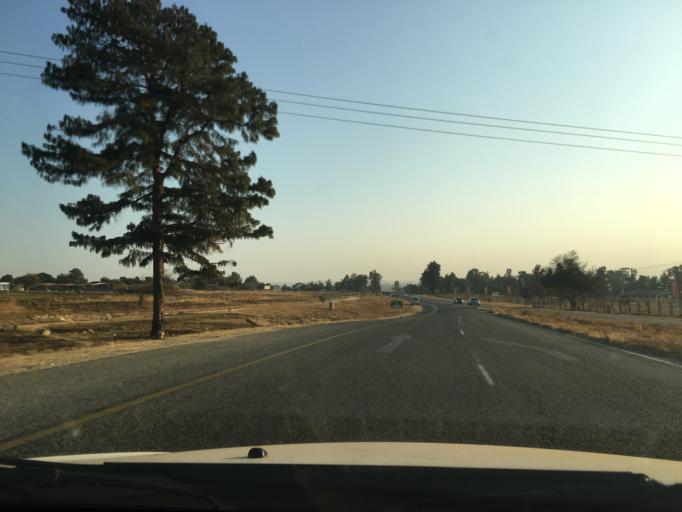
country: ZA
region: Gauteng
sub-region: West Rand District Municipality
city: Muldersdriseloop
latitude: -26.0170
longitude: 27.8590
